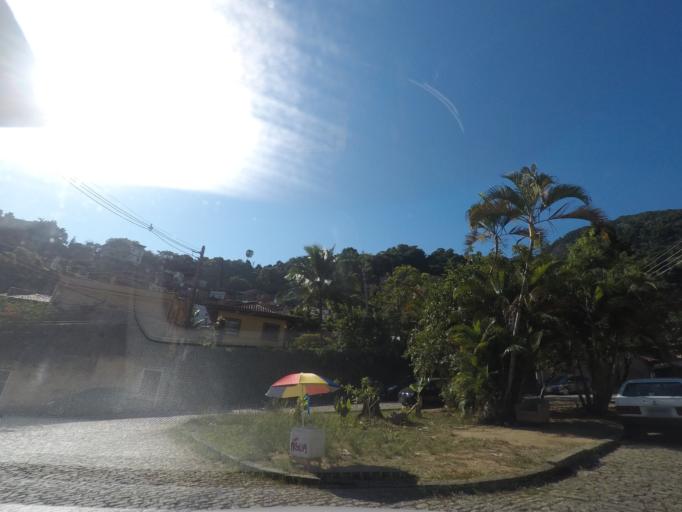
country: BR
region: Rio de Janeiro
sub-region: Rio De Janeiro
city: Rio de Janeiro
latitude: -22.9424
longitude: -43.2062
